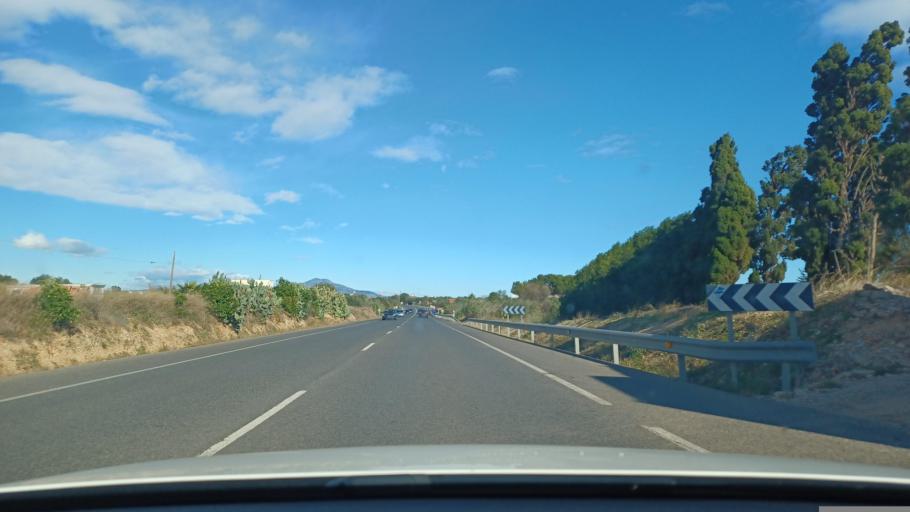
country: ES
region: Valencia
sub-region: Provincia de Castello
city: Benicarlo
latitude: 40.4453
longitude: 0.4472
